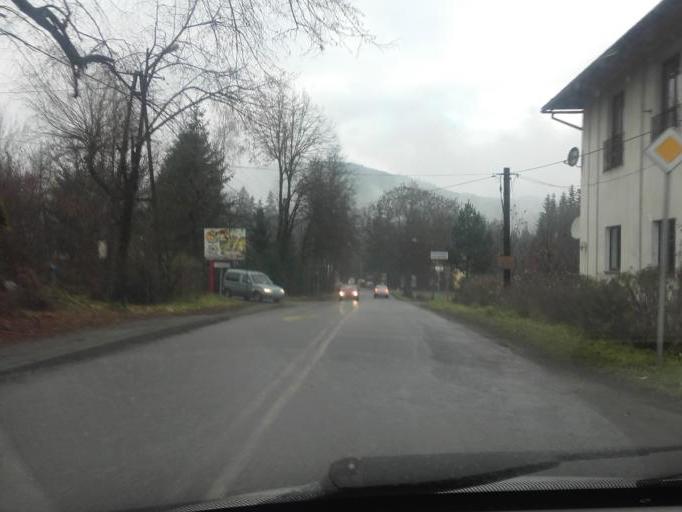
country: PL
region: Silesian Voivodeship
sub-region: Powiat cieszynski
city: Istebna
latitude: 49.5689
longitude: 18.8911
